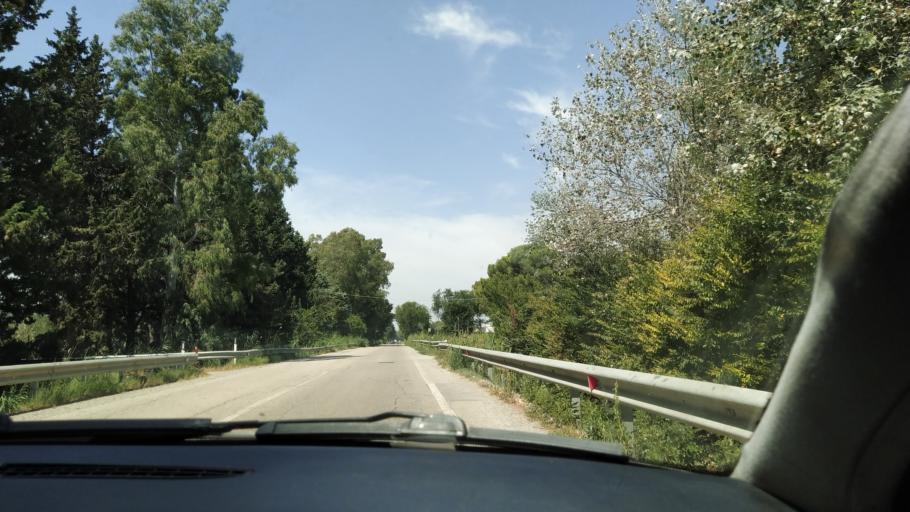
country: IT
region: Apulia
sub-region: Provincia di Taranto
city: Marina di Ginosa
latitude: 40.3726
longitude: 16.8047
